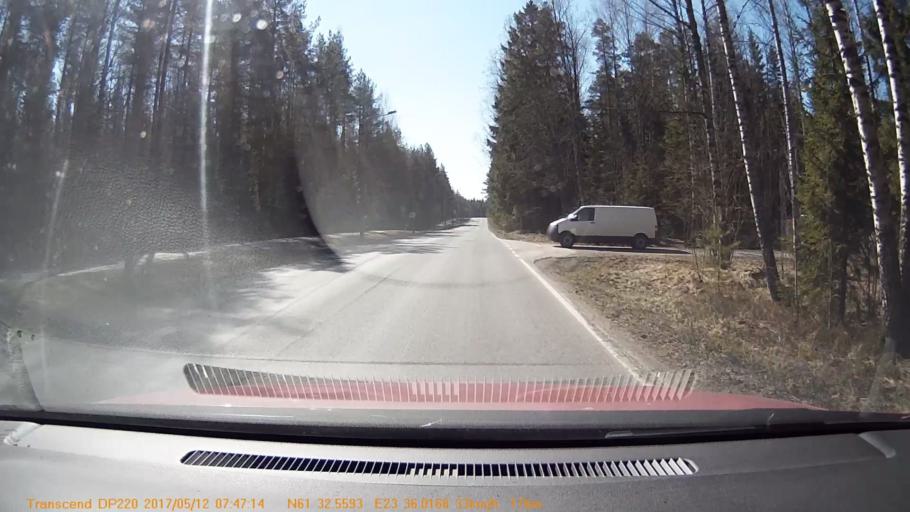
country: FI
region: Pirkanmaa
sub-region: Tampere
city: Yloejaervi
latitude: 61.5427
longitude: 23.6002
